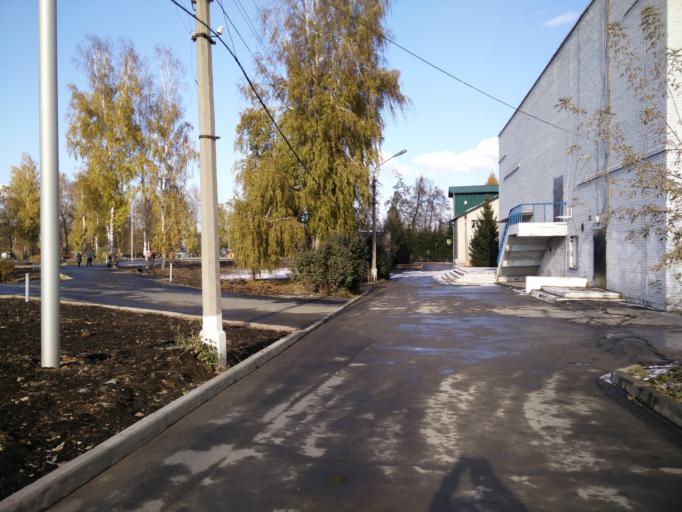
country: RU
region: Novosibirsk
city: Berdsk
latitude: 54.7565
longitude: 83.1027
